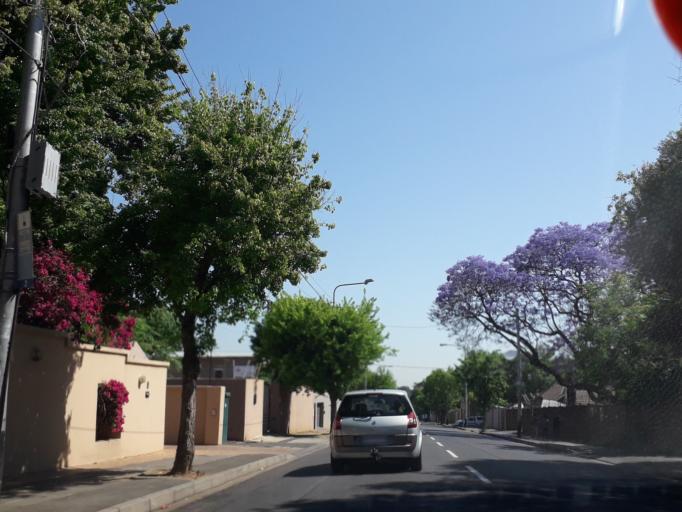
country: ZA
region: Gauteng
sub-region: City of Johannesburg Metropolitan Municipality
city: Johannesburg
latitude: -26.1549
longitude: 28.0768
